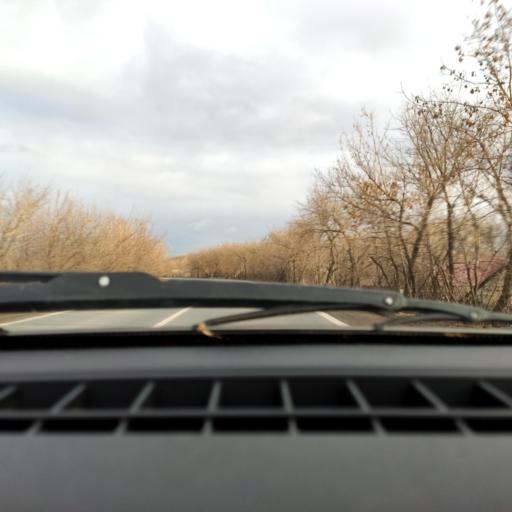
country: RU
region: Bashkortostan
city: Iglino
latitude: 54.7751
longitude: 56.2413
